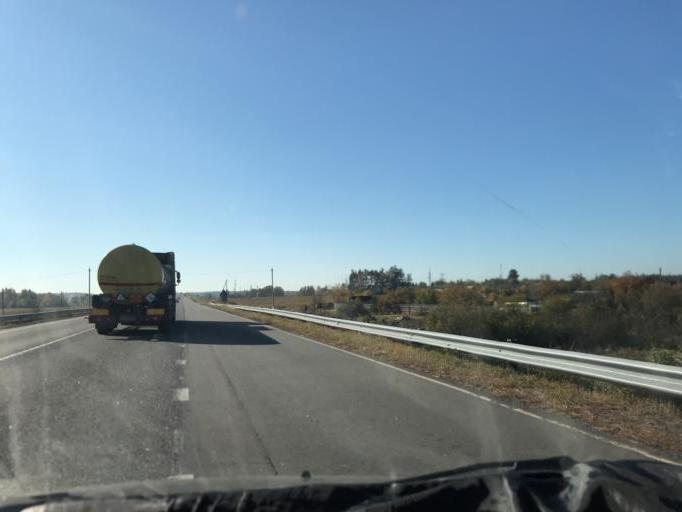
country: BY
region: Mogilev
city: Babruysk
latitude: 53.1886
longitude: 29.0508
